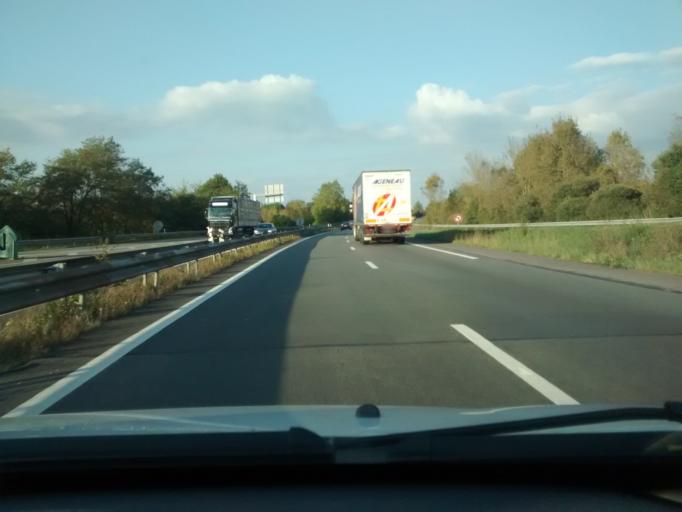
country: FR
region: Pays de la Loire
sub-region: Departement de la Loire-Atlantique
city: Heric
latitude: 47.4174
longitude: -1.6418
